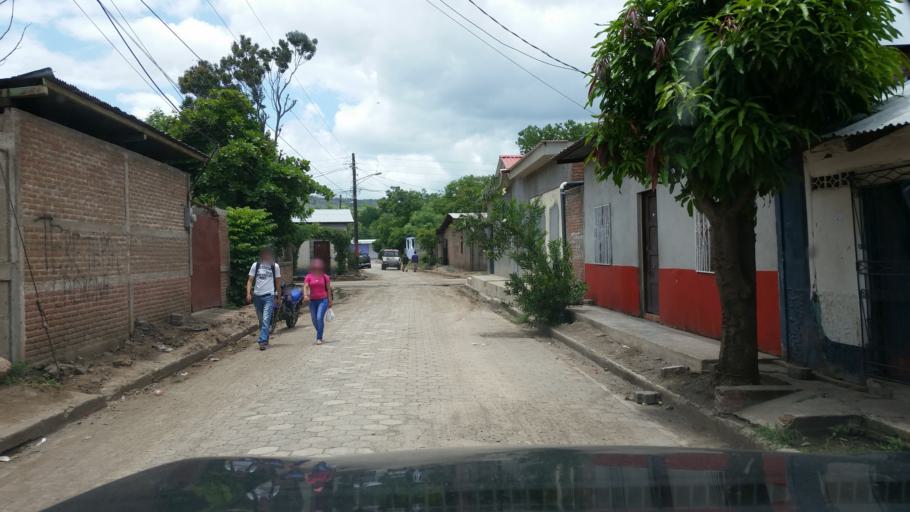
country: NI
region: Matagalpa
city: Ciudad Dario
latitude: 12.8490
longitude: -86.0973
